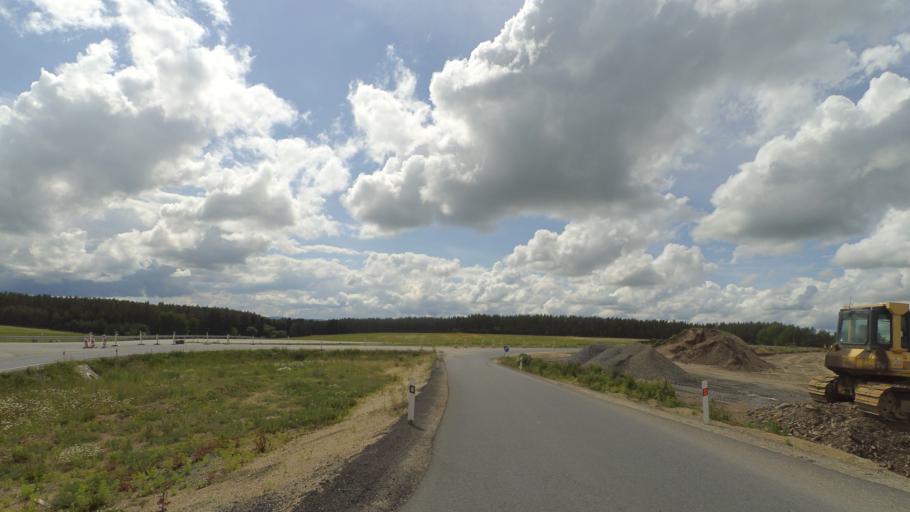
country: CZ
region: Plzensky
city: Bor
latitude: 49.7807
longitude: 12.7729
